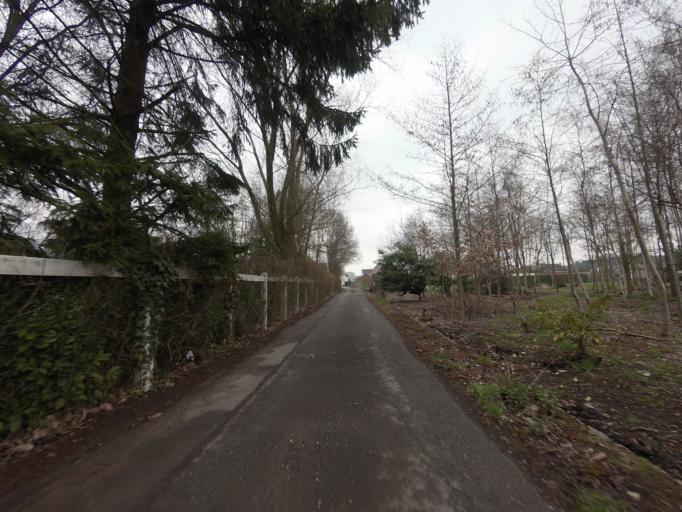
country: BE
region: Flanders
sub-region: Provincie Antwerpen
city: Putte
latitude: 51.0578
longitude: 4.5903
